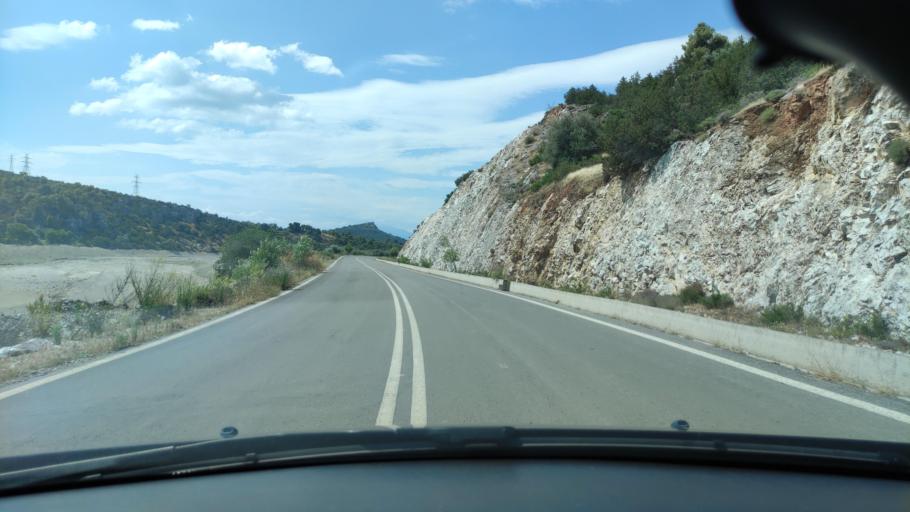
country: GR
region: Central Greece
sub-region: Nomos Evvoias
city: Afration
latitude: 38.4695
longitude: 23.6849
